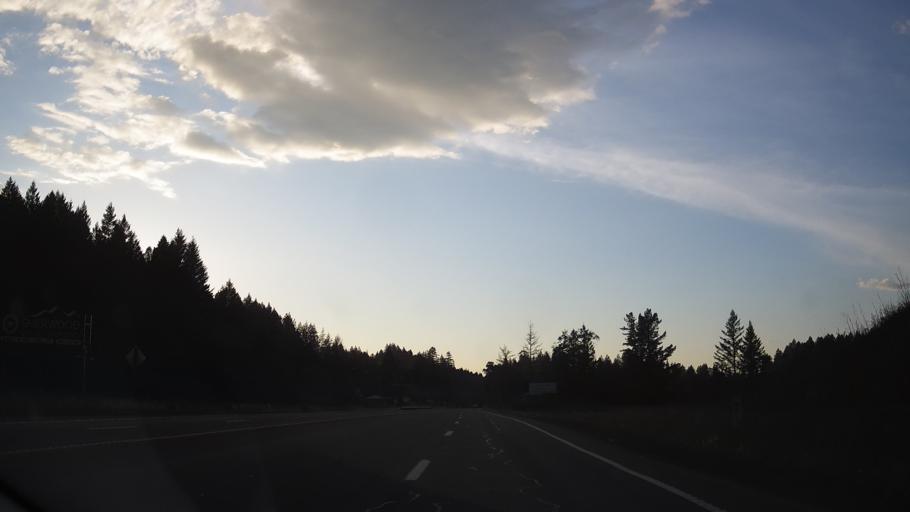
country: US
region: California
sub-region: Mendocino County
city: Willits
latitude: 39.3415
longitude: -123.3152
